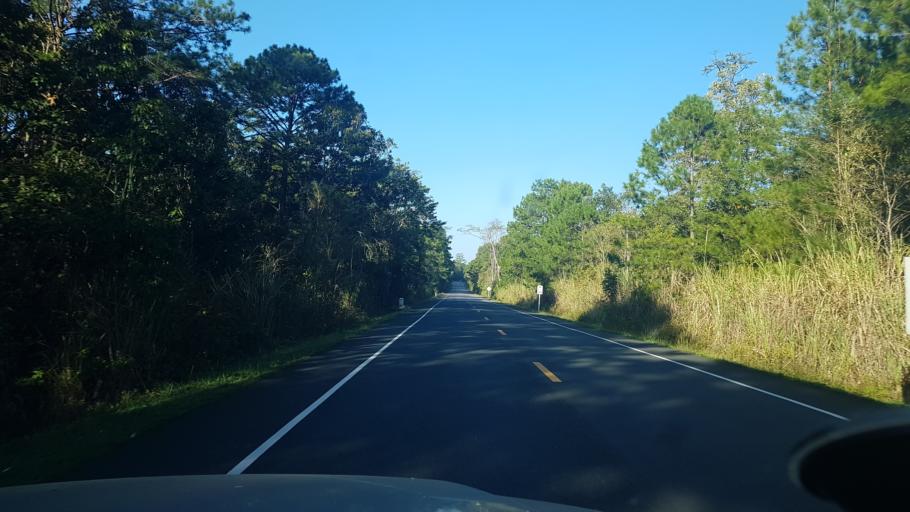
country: TH
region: Phetchabun
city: Nam Nao
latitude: 16.7259
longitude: 101.5797
